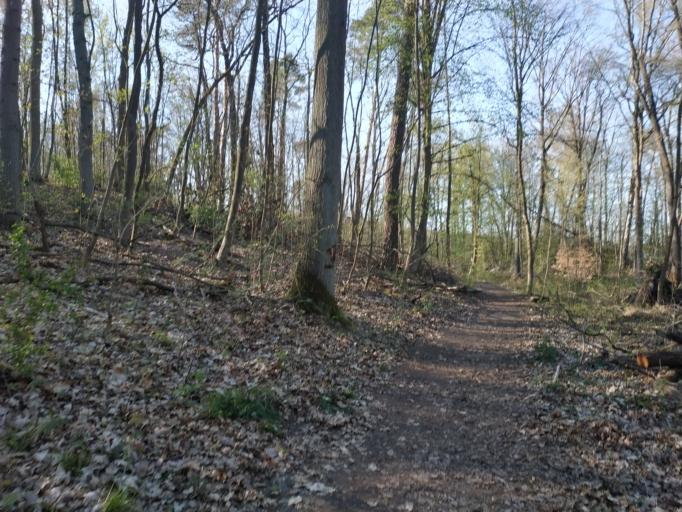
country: DE
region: Brandenburg
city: Petershagen
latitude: 52.5652
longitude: 13.8278
